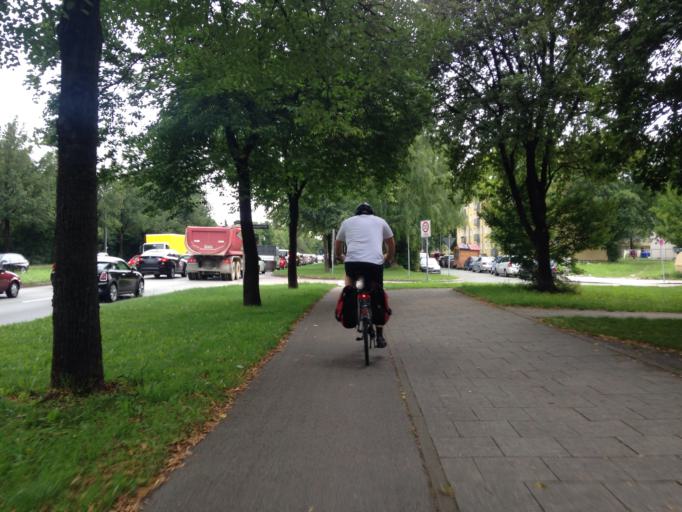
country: DE
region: Bavaria
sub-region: Upper Bavaria
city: Oberschleissheim
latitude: 48.1996
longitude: 11.5849
